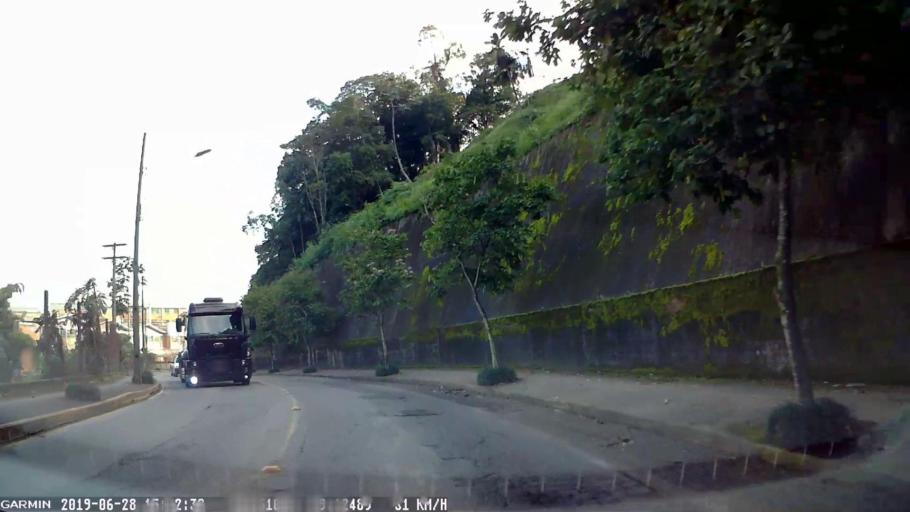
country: BR
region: Santa Catarina
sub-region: Jaragua Do Sul
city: Jaragua do Sul
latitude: -26.5110
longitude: -49.1250
